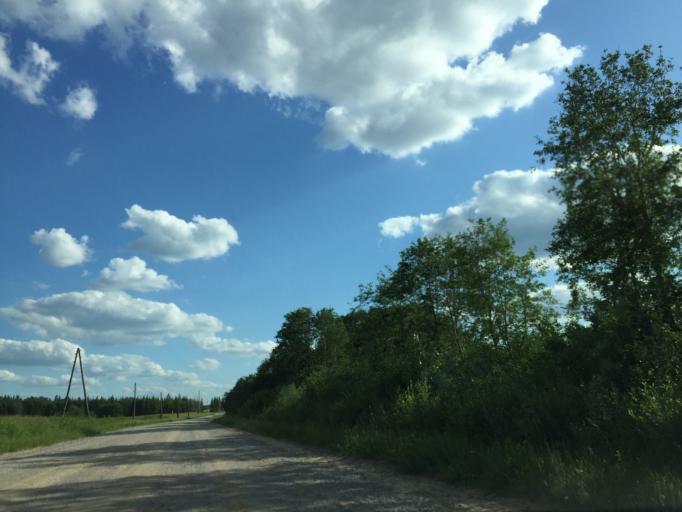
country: LV
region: Kandava
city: Kandava
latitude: 56.8931
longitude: 22.7878
